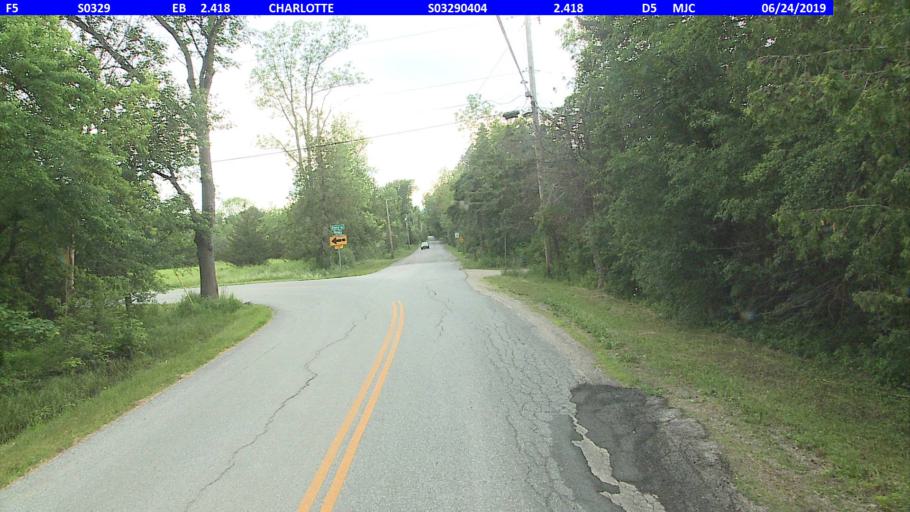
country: US
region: Vermont
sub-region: Addison County
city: Vergennes
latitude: 44.3061
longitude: -73.2935
